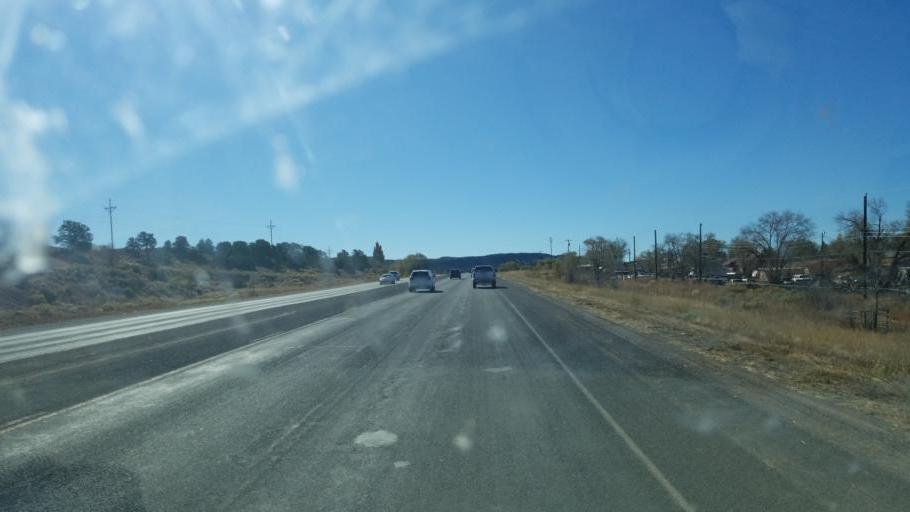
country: US
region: Arizona
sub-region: Apache County
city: Window Rock
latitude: 35.6764
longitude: -109.0609
